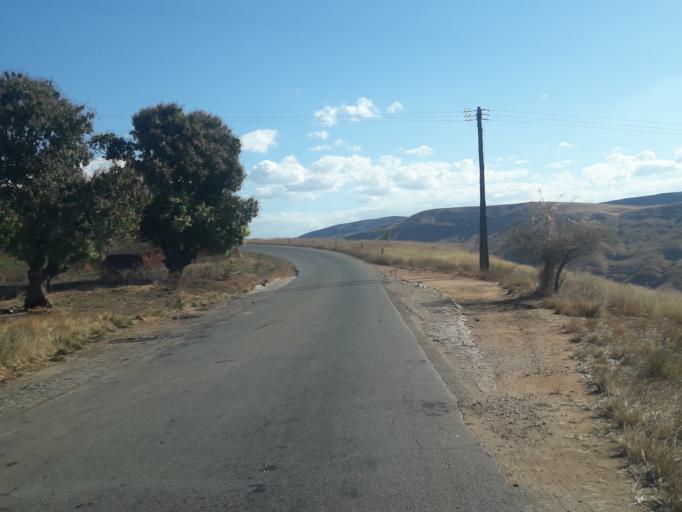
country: MG
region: Analamanga
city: Ankazobe
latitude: -17.7020
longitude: 46.9895
